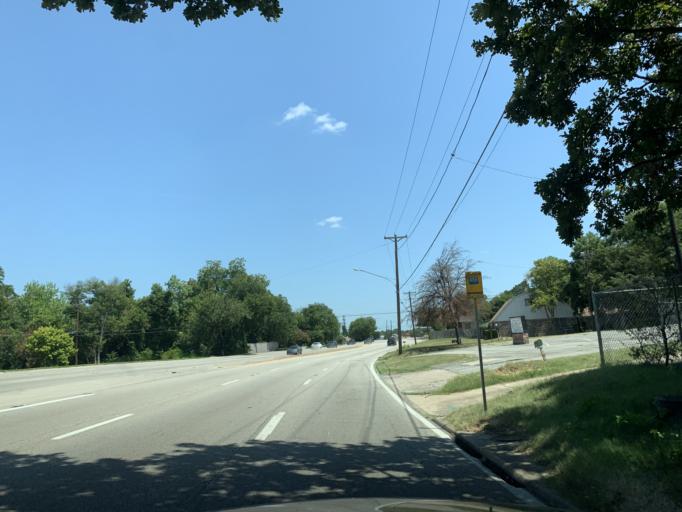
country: US
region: Texas
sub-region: Dallas County
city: Cockrell Hill
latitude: 32.6836
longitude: -96.8102
